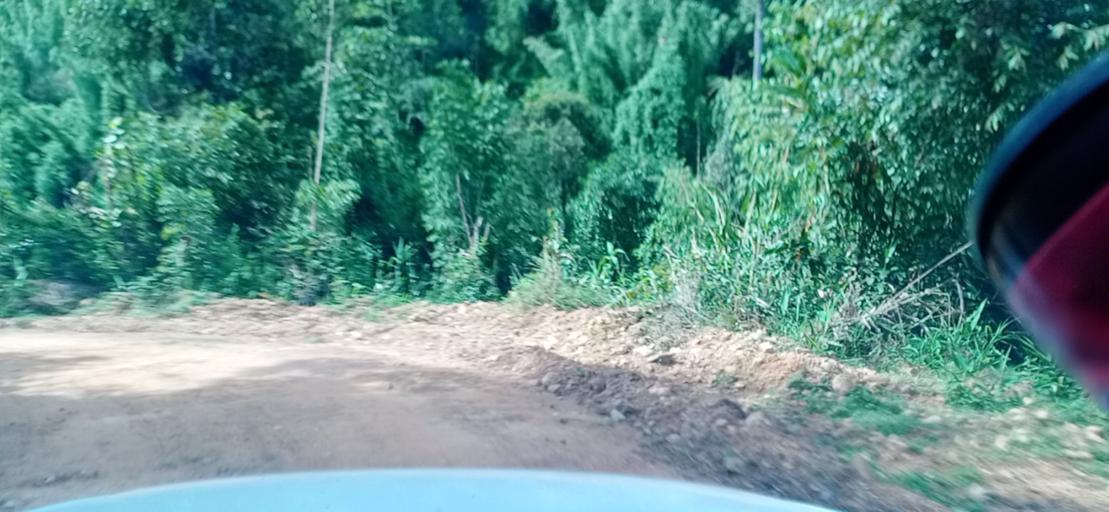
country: TH
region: Changwat Bueng Kan
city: Pak Khat
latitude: 18.6371
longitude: 103.2586
